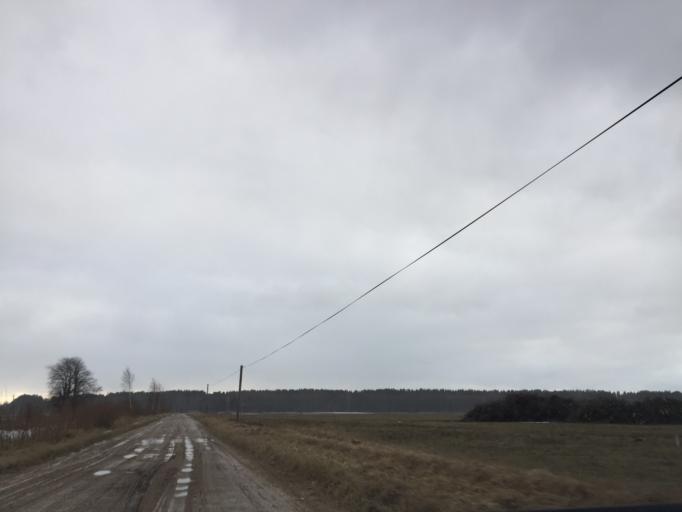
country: LV
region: Salacgrivas
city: Salacgriva
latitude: 57.6449
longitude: 24.3909
